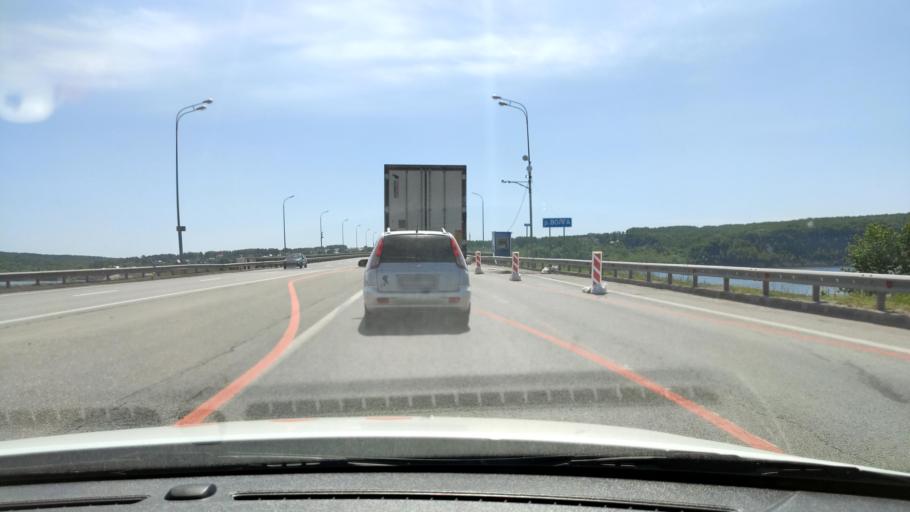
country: RU
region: Tatarstan
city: Osinovo
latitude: 55.7909
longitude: 48.8404
